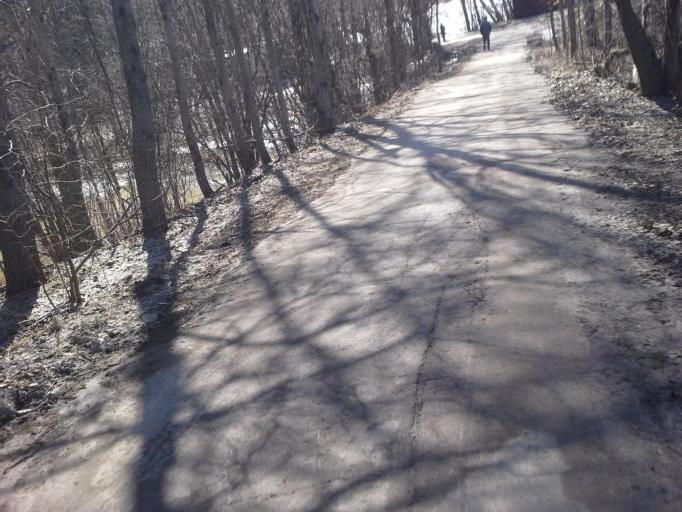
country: RU
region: Moscow
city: Yasenevo
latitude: 55.5866
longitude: 37.5465
